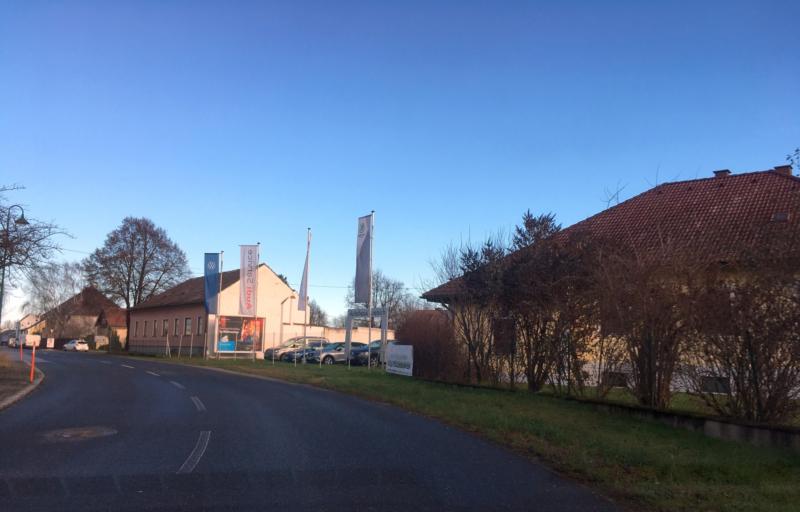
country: AT
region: Lower Austria
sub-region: Politischer Bezirk Bruck an der Leitha
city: Petronell-Carnuntum
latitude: 48.1474
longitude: 16.8342
